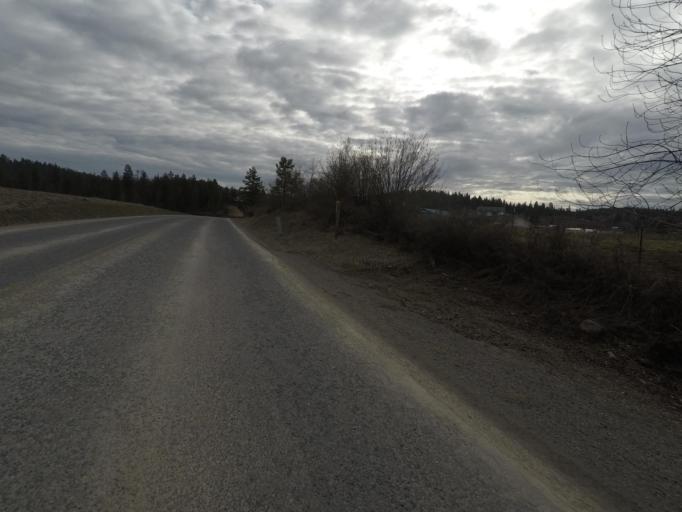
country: US
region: Washington
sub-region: Stevens County
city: Colville
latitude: 48.5182
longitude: -117.8721
